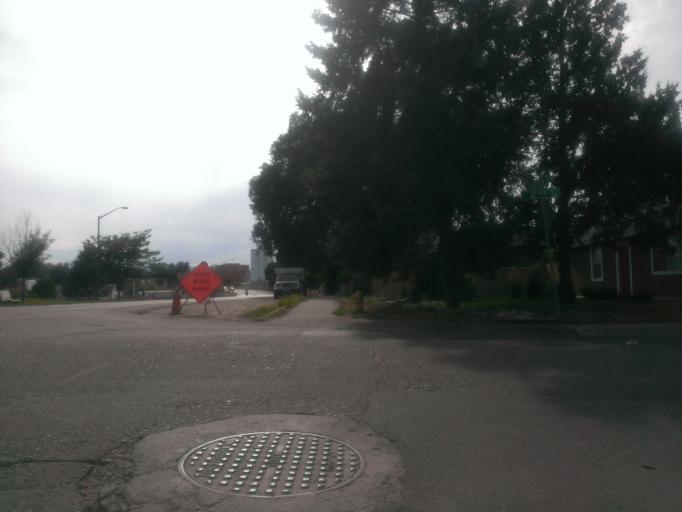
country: US
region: Colorado
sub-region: Larimer County
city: Fort Collins
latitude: 40.5889
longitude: -105.0660
